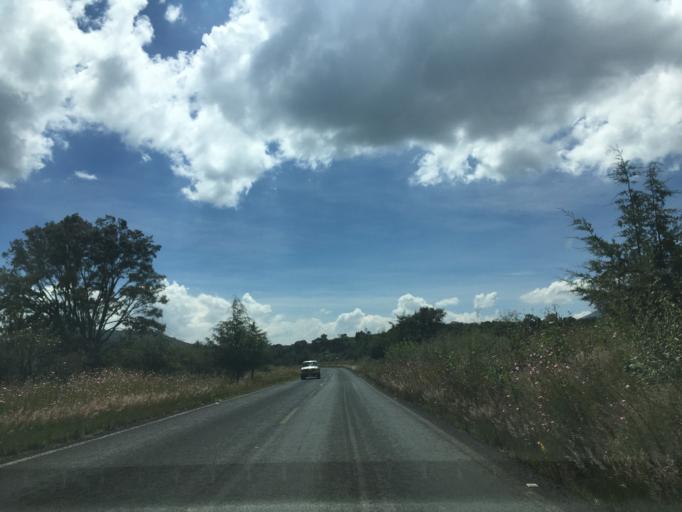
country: MX
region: Michoacan
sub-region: Morelia
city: Cuto de la Esperanza
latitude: 19.7276
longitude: -101.3458
